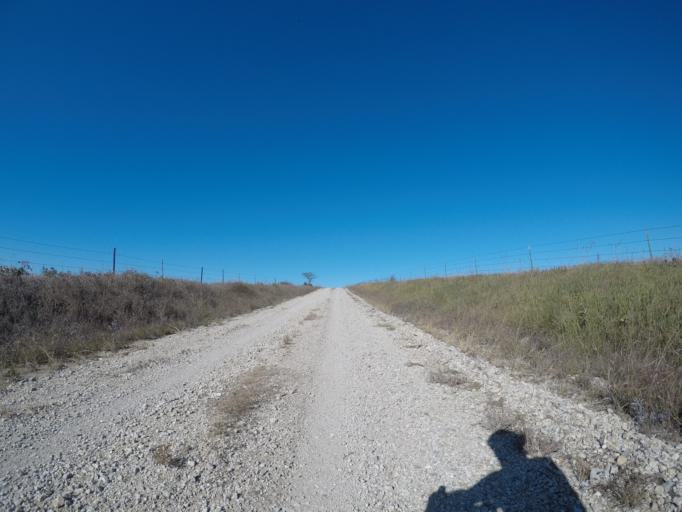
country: US
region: Kansas
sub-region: Wabaunsee County
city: Alma
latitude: 38.9159
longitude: -96.3871
